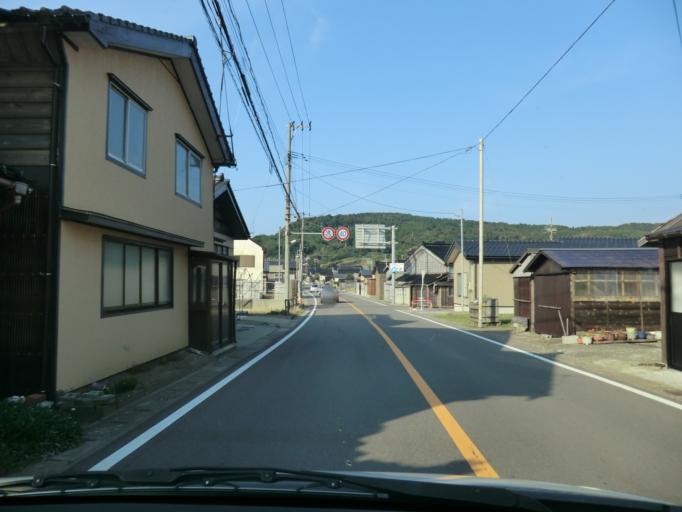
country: JP
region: Niigata
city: Kashiwazaki
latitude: 37.4748
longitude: 138.6184
